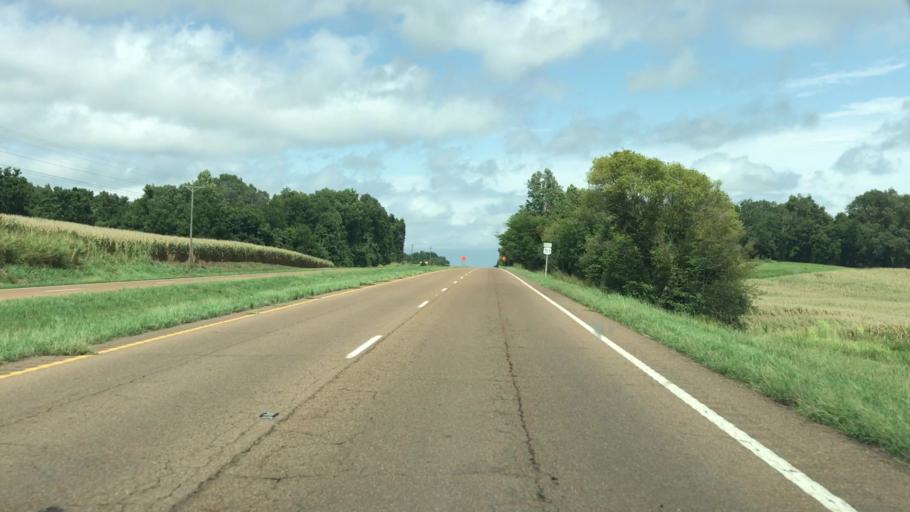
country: US
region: Tennessee
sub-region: Obion County
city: Englewood
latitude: 36.3714
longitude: -89.1218
